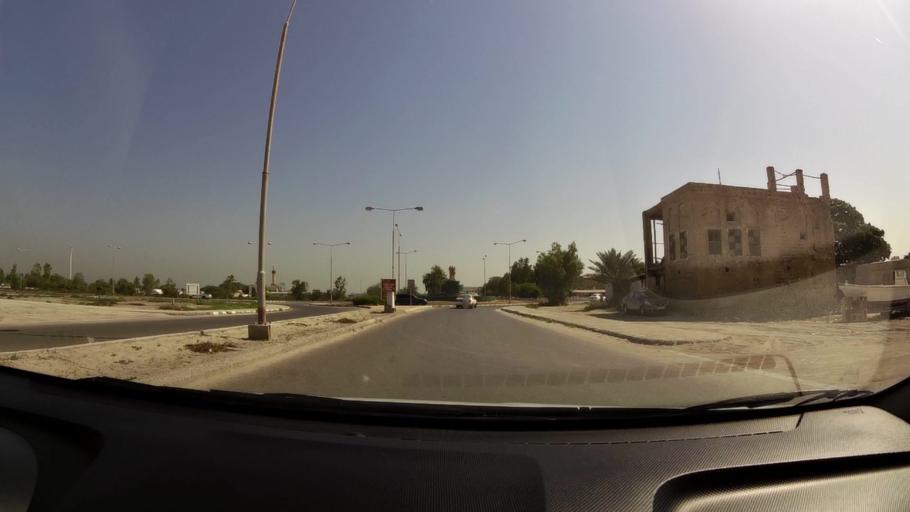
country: AE
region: Umm al Qaywayn
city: Umm al Qaywayn
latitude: 25.5843
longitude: 55.5687
